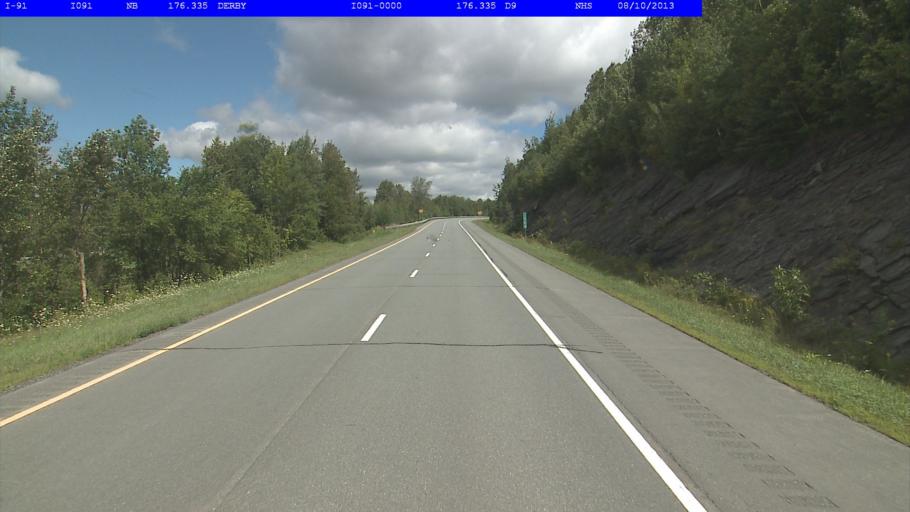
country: US
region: Vermont
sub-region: Orleans County
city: Newport
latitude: 44.9945
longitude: -72.1018
